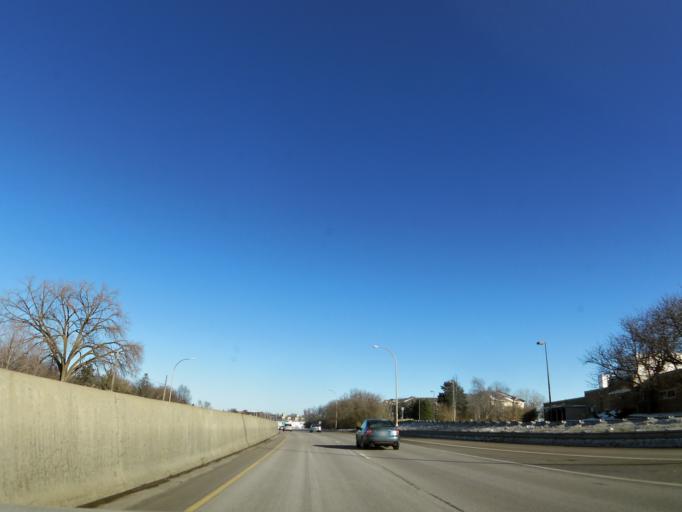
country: US
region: Minnesota
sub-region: Hennepin County
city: Saint Louis Park
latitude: 44.9401
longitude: -93.3541
